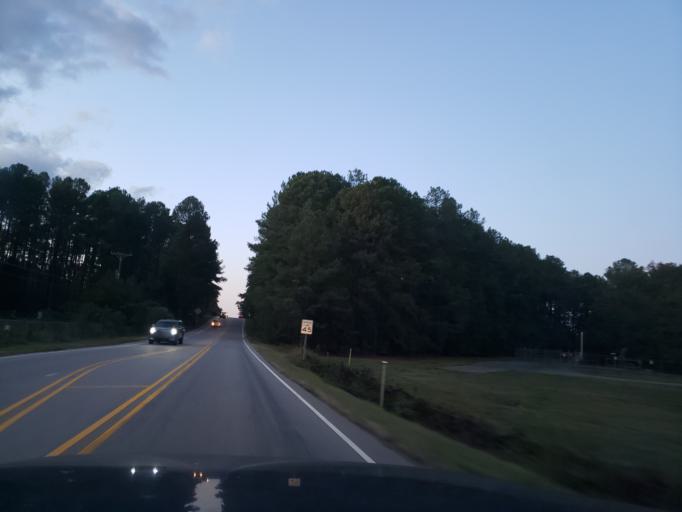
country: US
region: North Carolina
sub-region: Orange County
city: Chapel Hill
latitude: 35.8938
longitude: -78.9583
